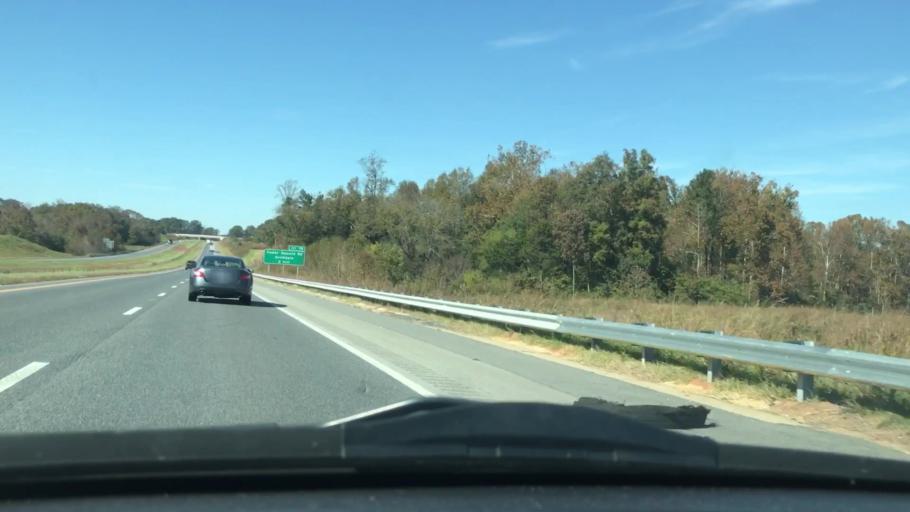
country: US
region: North Carolina
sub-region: Randolph County
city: Randleman
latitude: 35.8482
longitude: -79.8715
